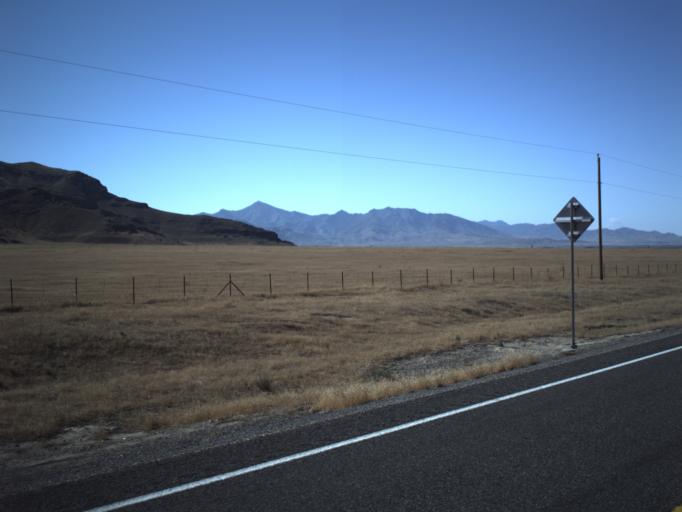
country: US
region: Utah
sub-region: Millard County
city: Delta
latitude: 39.6159
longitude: -112.3171
